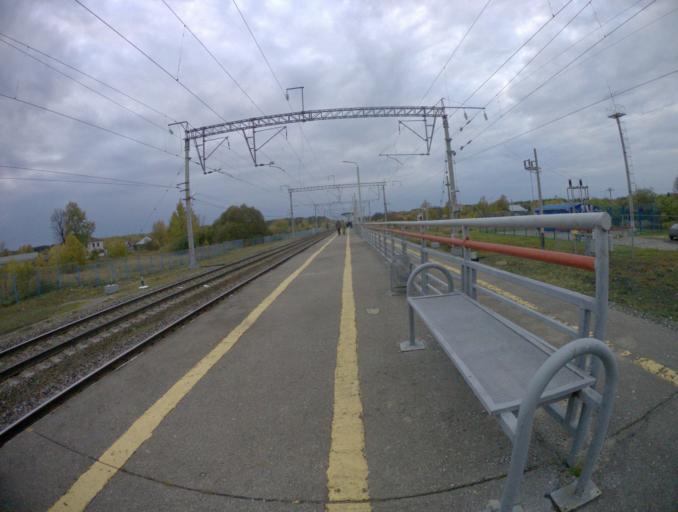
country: RU
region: Vladimir
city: Mstera
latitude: 56.2651
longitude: 41.8655
